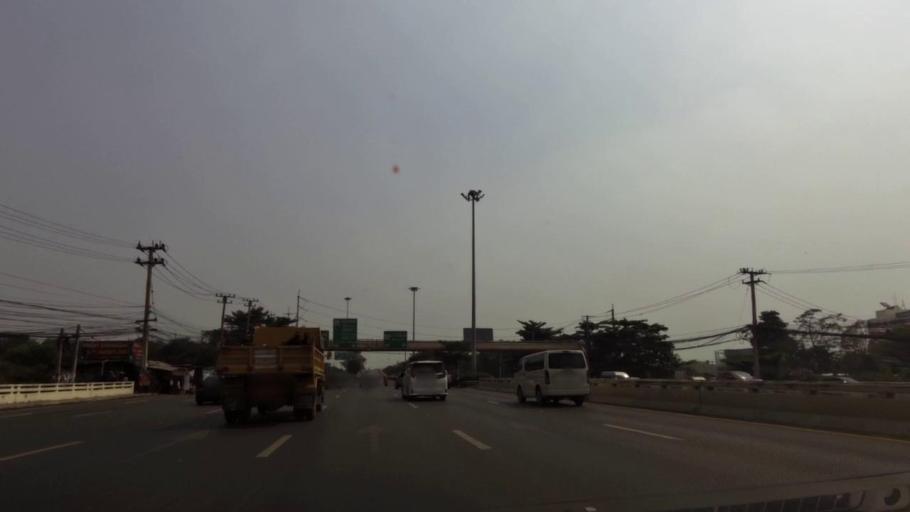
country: TH
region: Phra Nakhon Si Ayutthaya
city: Phra Nakhon Si Ayutthaya
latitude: 14.3439
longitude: 100.6096
